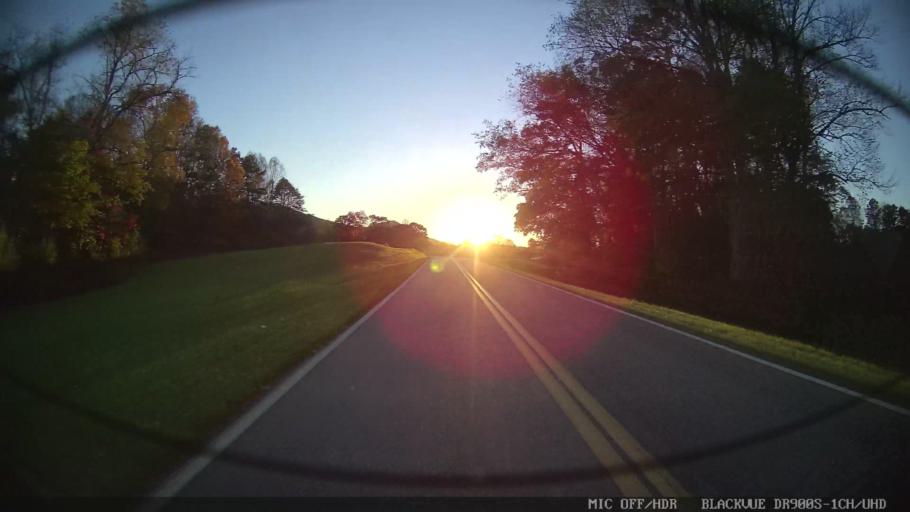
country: US
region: Georgia
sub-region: Union County
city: Blairsville
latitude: 34.8457
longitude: -83.9305
